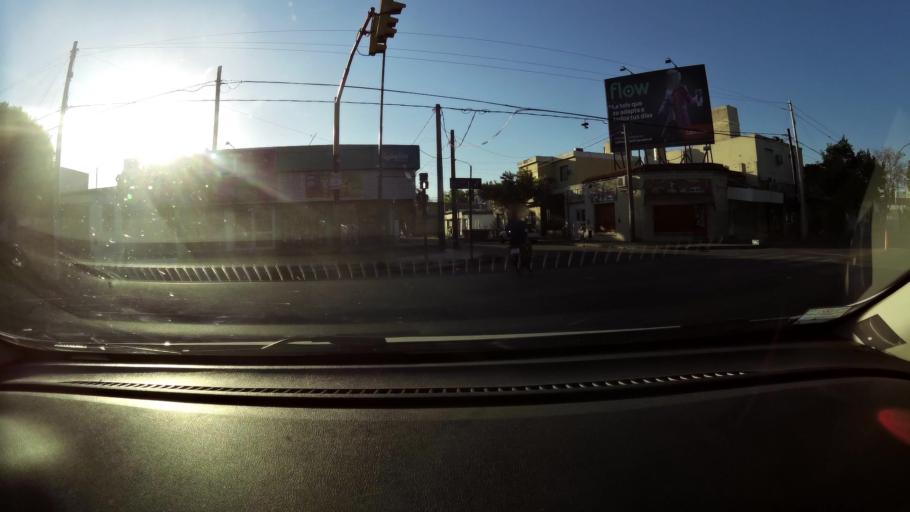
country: AR
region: Cordoba
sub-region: Departamento de Capital
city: Cordoba
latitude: -31.3731
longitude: -64.2061
